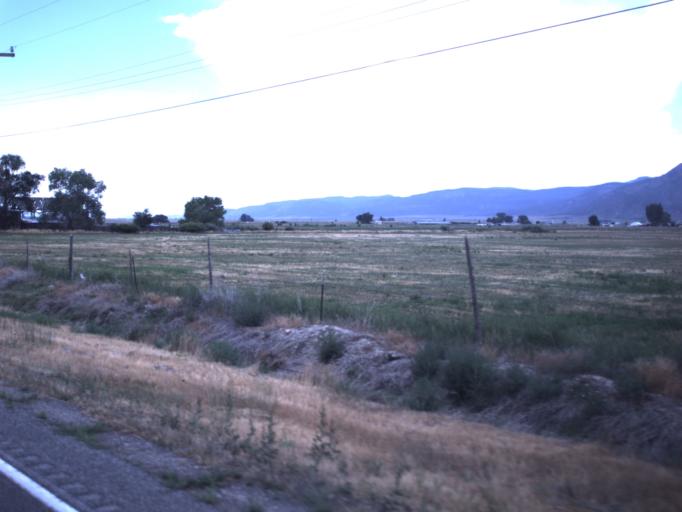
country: US
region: Utah
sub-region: Sanpete County
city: Moroni
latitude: 39.4744
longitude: -111.5629
